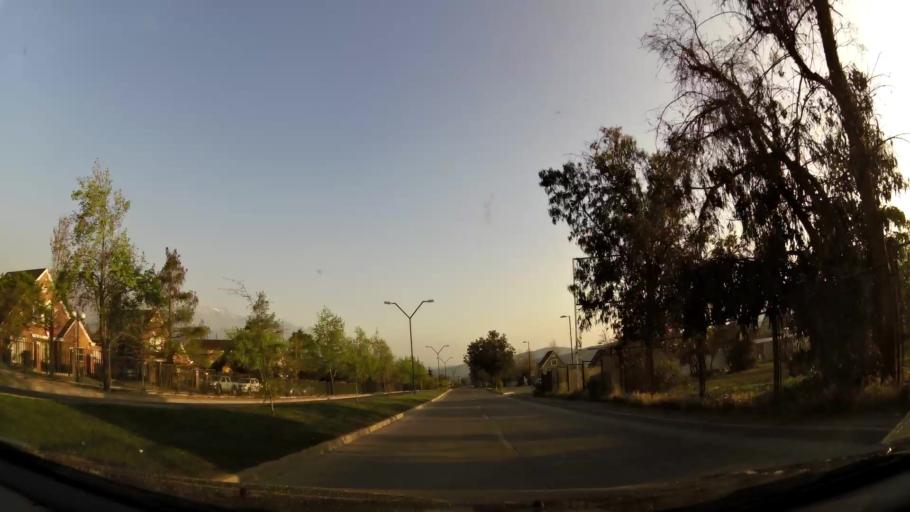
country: CL
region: Santiago Metropolitan
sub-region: Provincia de Chacabuco
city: Chicureo Abajo
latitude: -33.3279
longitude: -70.5195
